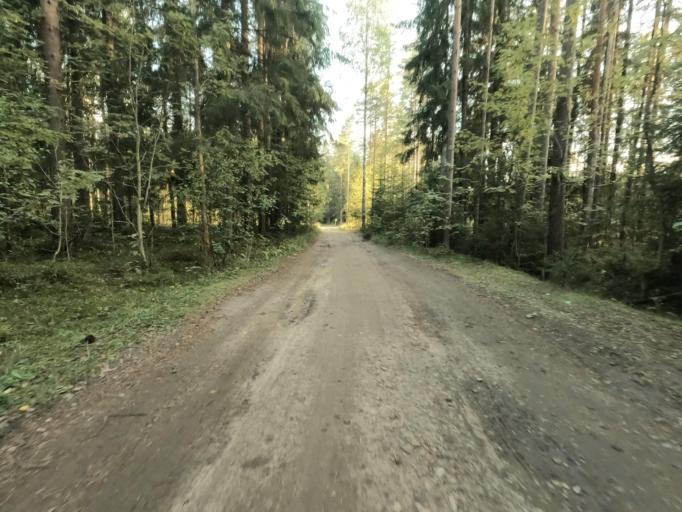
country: RU
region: Leningrad
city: Otradnoye
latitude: 59.8242
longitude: 30.7725
